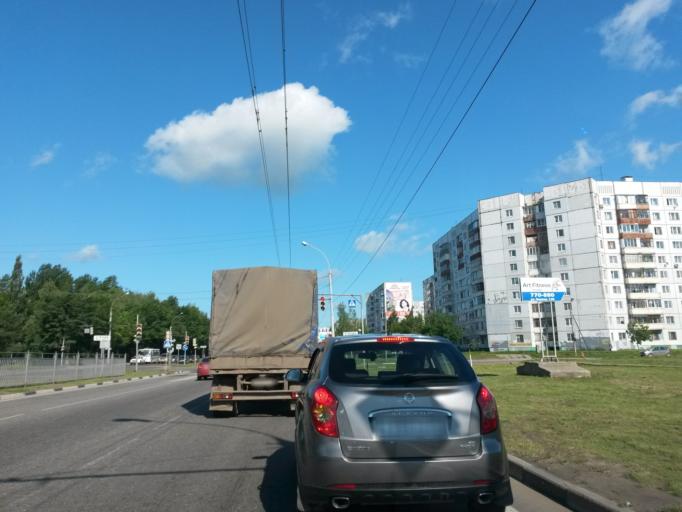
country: RU
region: Jaroslavl
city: Yaroslavl
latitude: 57.6906
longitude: 39.7767
